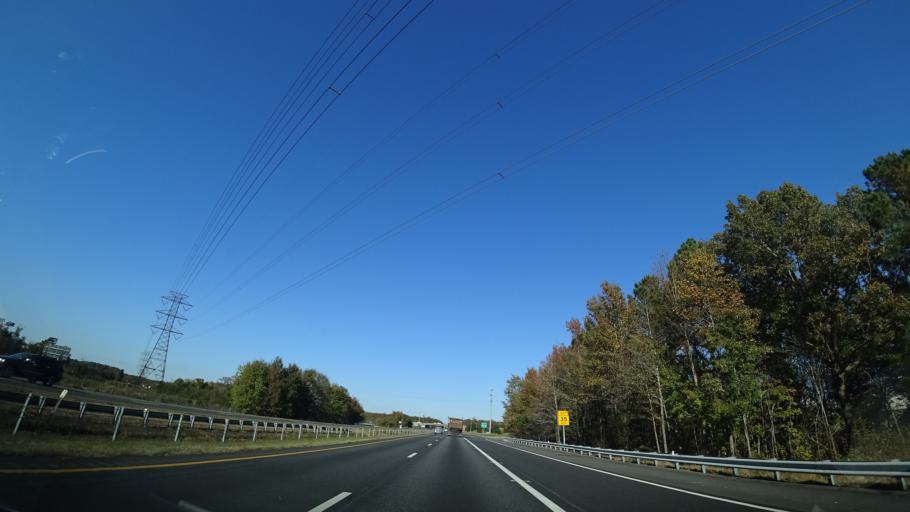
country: US
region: Virginia
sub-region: City of Portsmouth
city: Portsmouth Heights
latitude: 36.8821
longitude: -76.4311
